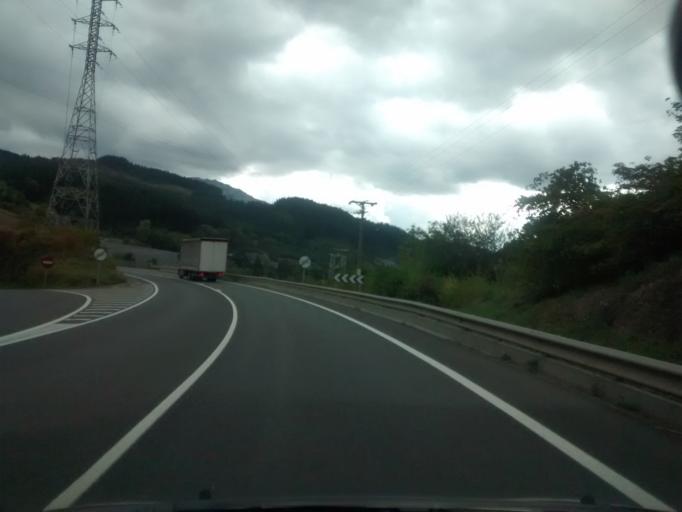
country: ES
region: Basque Country
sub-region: Provincia de Guipuzcoa
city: Arrasate / Mondragon
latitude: 43.0575
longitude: -2.4918
